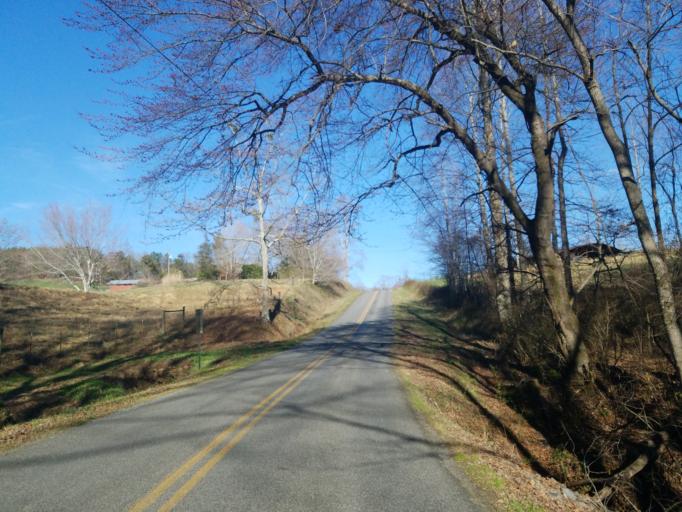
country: US
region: Georgia
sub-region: Gilmer County
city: Ellijay
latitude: 34.6353
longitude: -84.3620
